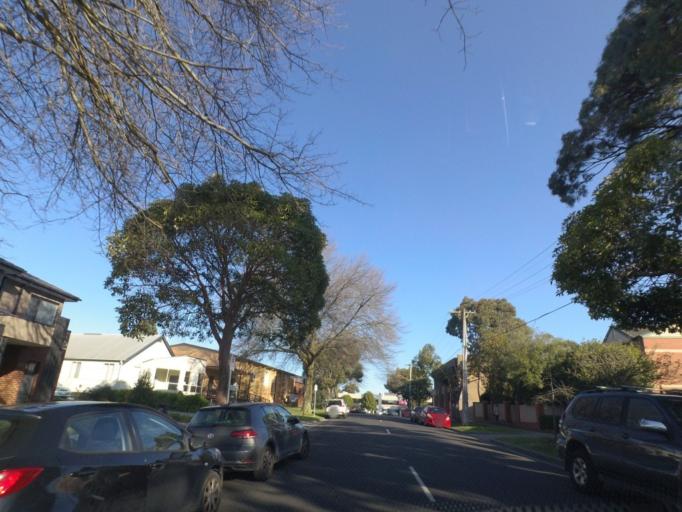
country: AU
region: Victoria
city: Mitcham
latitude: -37.8149
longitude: 145.1960
